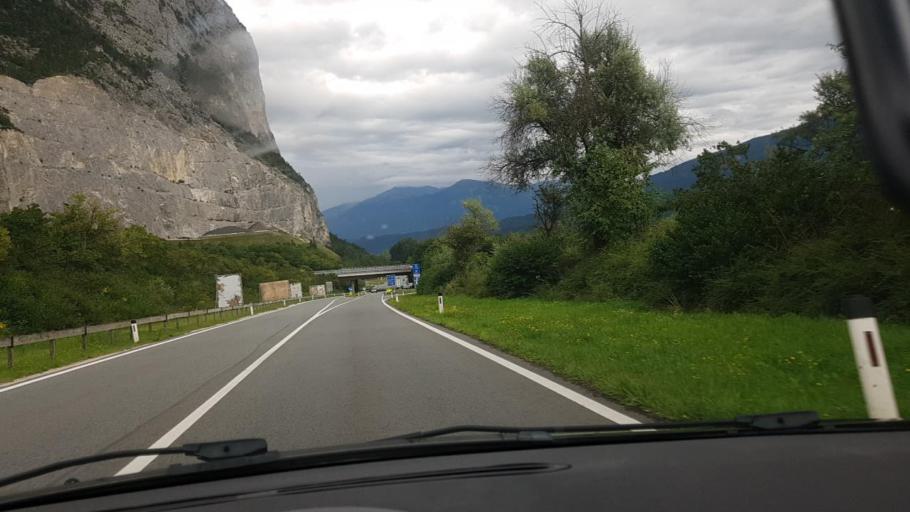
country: AT
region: Tyrol
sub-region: Politischer Bezirk Innsbruck Land
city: Unterperfuss
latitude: 47.2707
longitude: 11.2552
